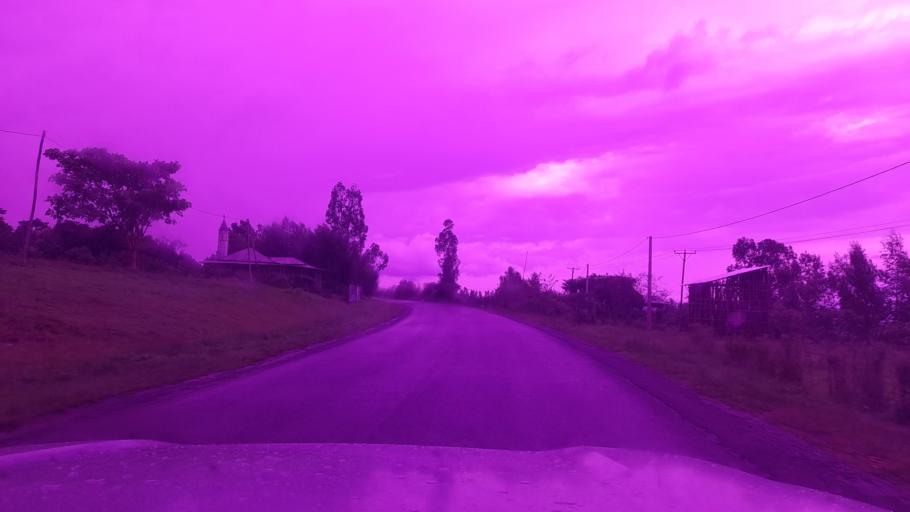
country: ET
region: Oromiya
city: Jima
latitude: 7.7063
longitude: 37.0697
